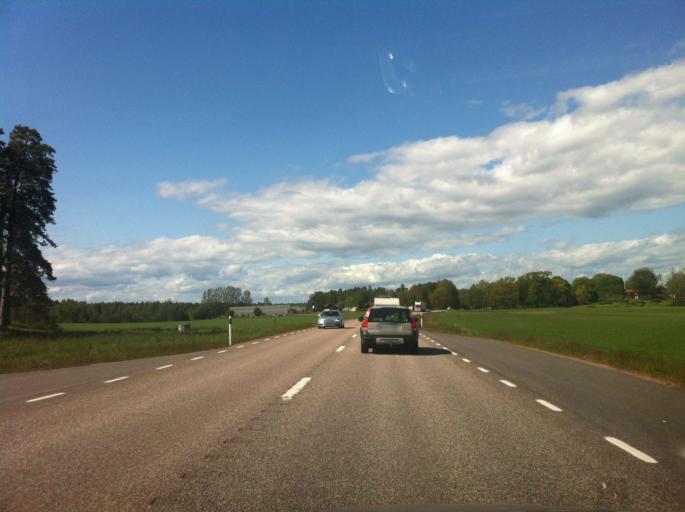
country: SE
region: Vaermland
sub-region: Kristinehamns Kommun
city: Bjorneborg
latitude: 59.1228
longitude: 14.1763
